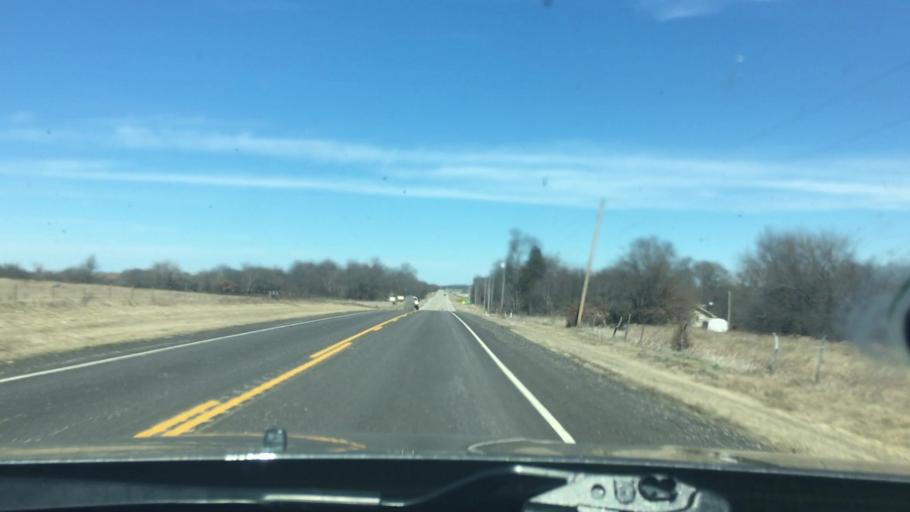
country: US
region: Oklahoma
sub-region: Murray County
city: Sulphur
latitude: 34.3580
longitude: -96.9509
